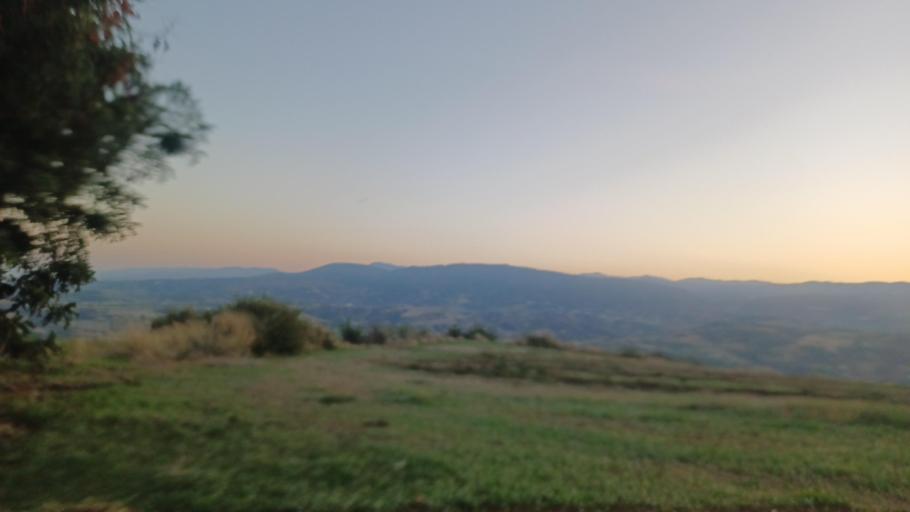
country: CY
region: Pafos
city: Polis
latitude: 34.9870
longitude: 32.4368
